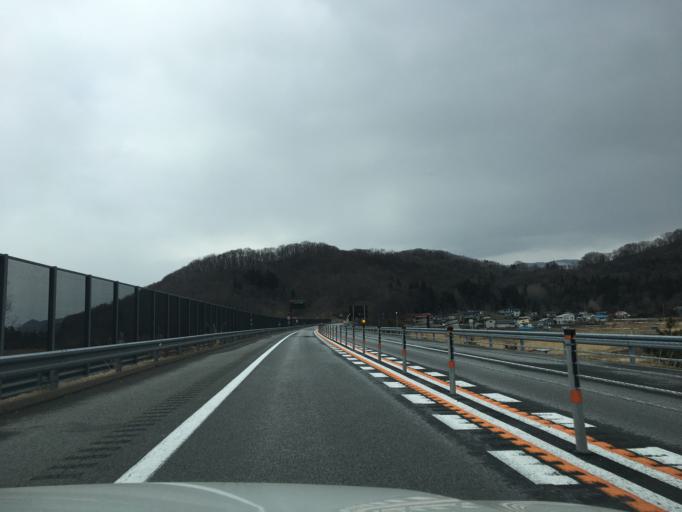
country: JP
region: Aomori
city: Aomori Shi
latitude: 40.8133
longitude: 140.8058
